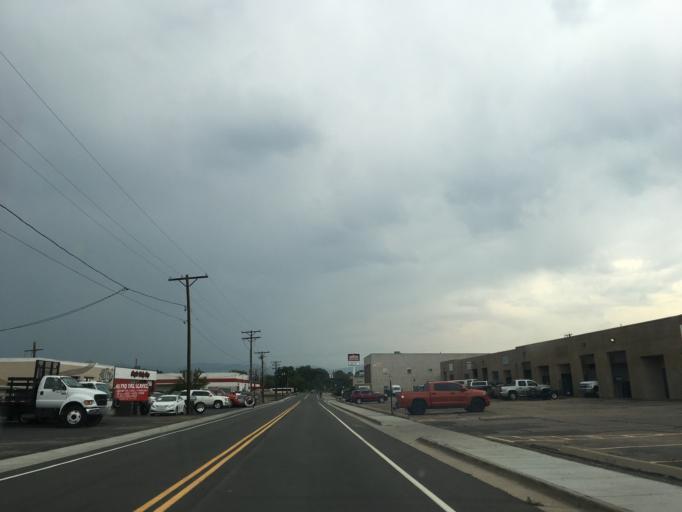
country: US
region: Colorado
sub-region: Arapahoe County
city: Sheridan
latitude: 39.6533
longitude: -105.0282
